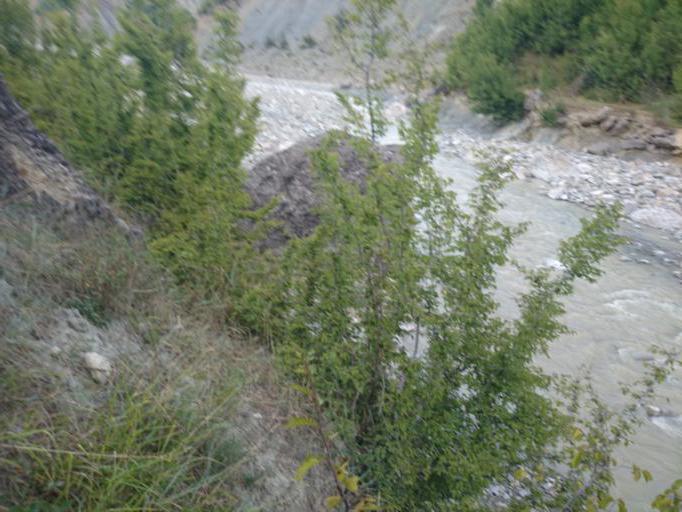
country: AL
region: Elbasan
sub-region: Rrethi i Gramshit
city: Porocan
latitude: 40.9350
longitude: 20.2697
